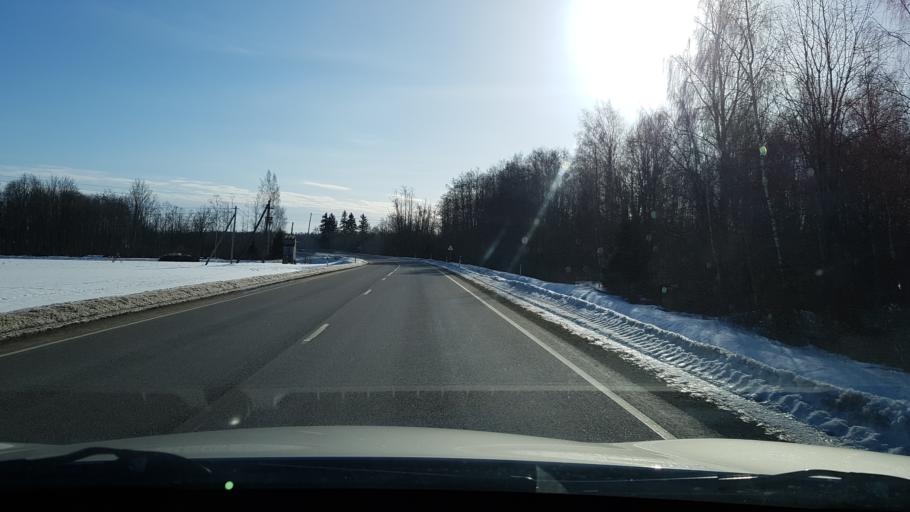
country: EE
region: Jogevamaa
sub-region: Poltsamaa linn
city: Poltsamaa
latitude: 58.6329
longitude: 25.7774
